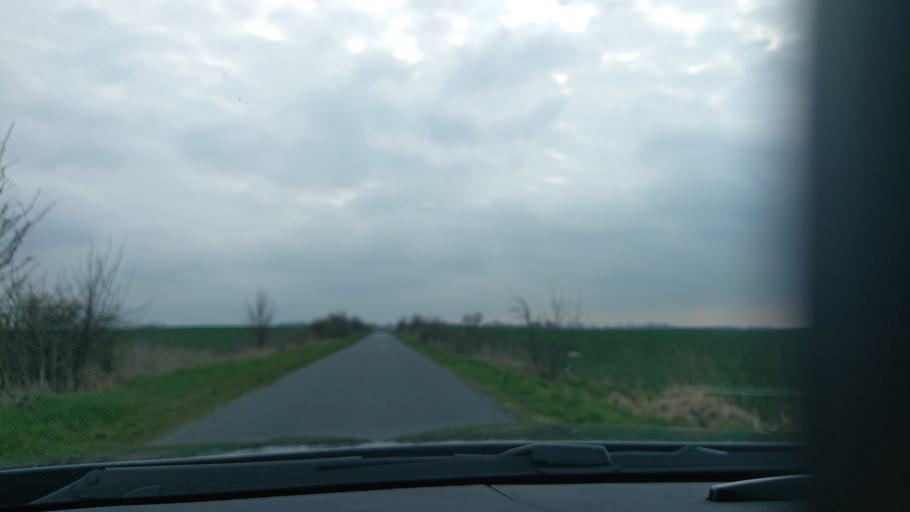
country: PL
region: Greater Poland Voivodeship
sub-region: Powiat gnieznienski
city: Gniezno
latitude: 52.5589
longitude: 17.5168
